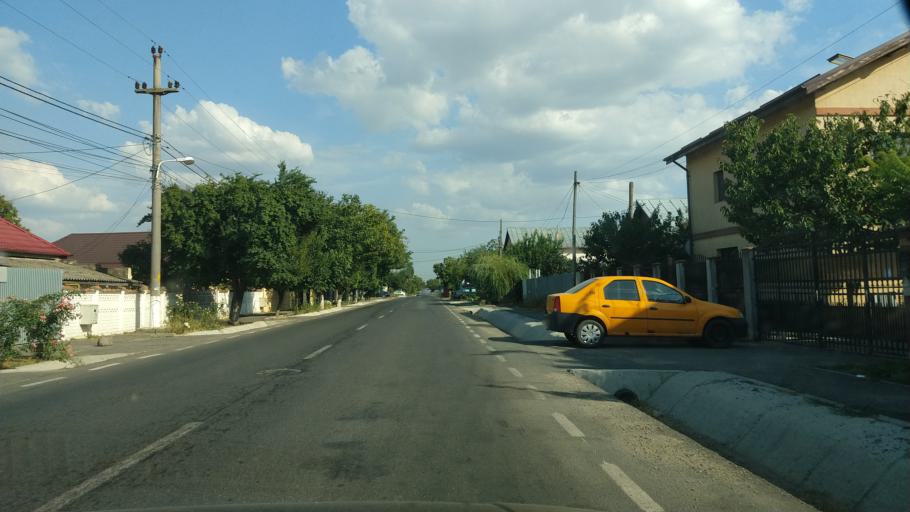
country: RO
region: Ilfov
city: Stefanestii de Jos
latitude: 44.5320
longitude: 26.2333
